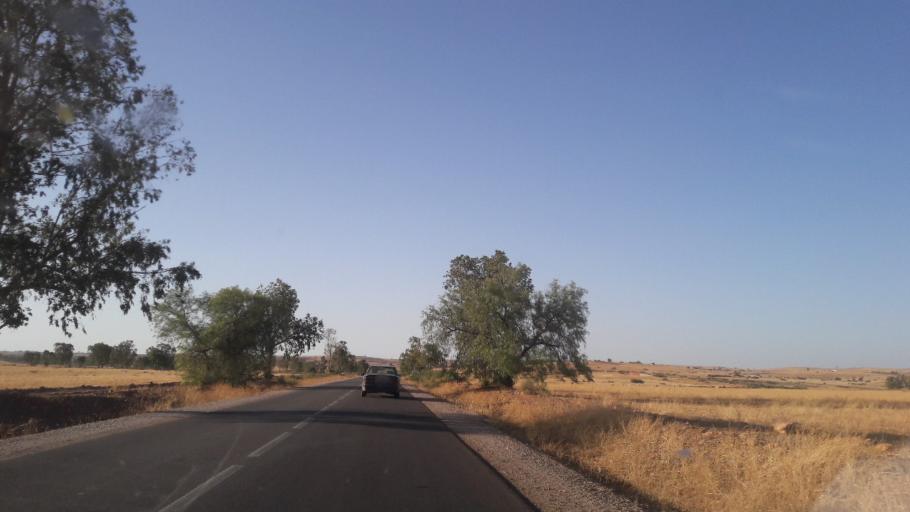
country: MA
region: Chaouia-Ouardigha
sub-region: Khouribga Province
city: Boujniba
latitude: 32.9925
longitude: -6.6828
